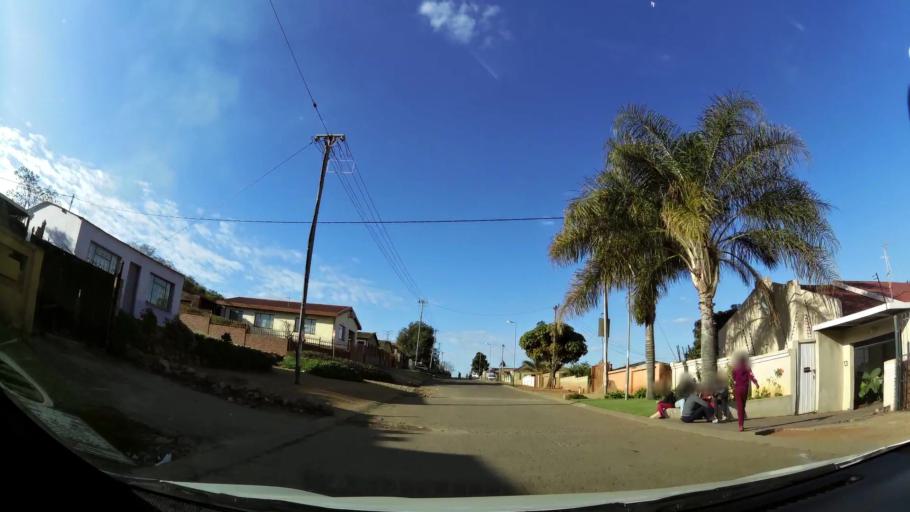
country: ZA
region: Gauteng
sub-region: City of Tshwane Metropolitan Municipality
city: Cullinan
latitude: -25.7026
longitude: 28.3869
